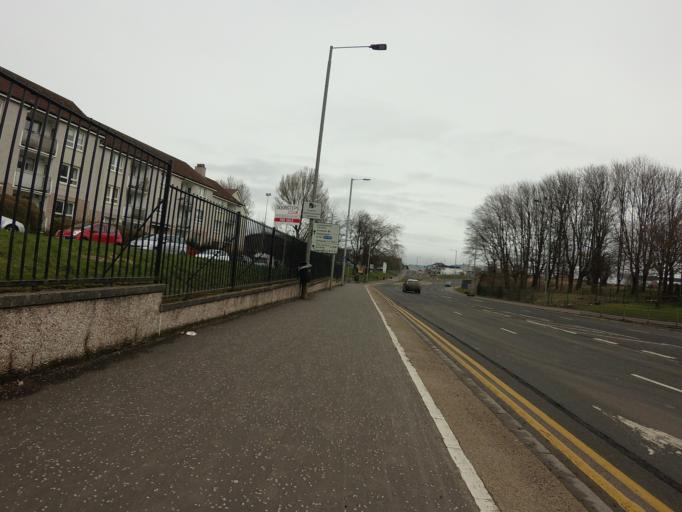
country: GB
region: Scotland
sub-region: South Lanarkshire
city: Rutherglen
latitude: 55.8301
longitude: -4.2482
